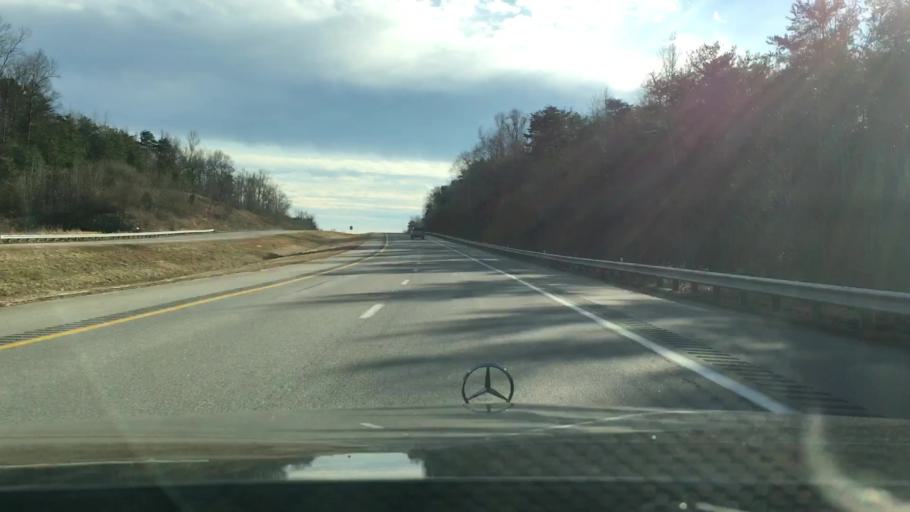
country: US
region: Virginia
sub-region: City of Danville
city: Danville
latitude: 36.6313
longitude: -79.3650
